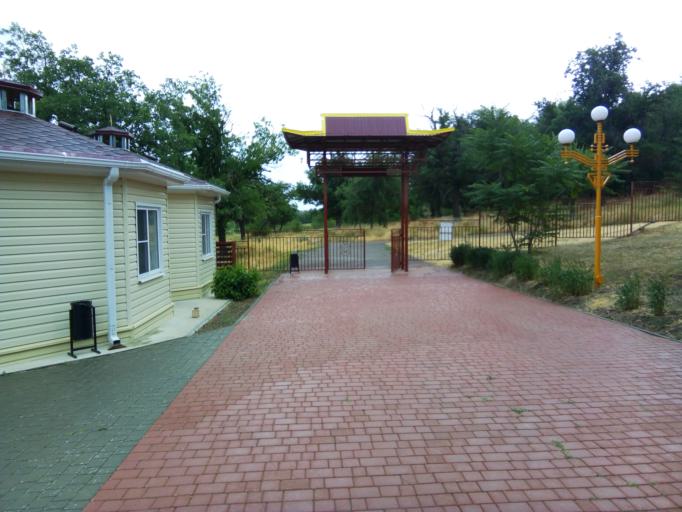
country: RU
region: Kalmykiya
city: Elista
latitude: 46.3063
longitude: 44.2475
